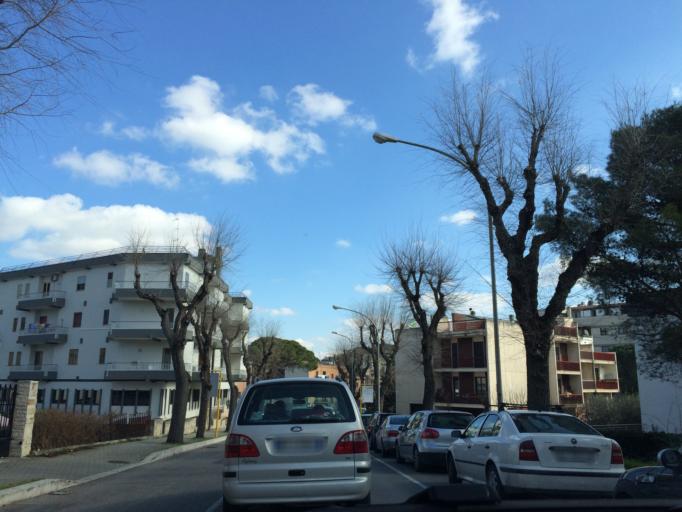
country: IT
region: Basilicate
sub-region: Provincia di Matera
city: Matera
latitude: 40.6645
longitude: 16.5964
